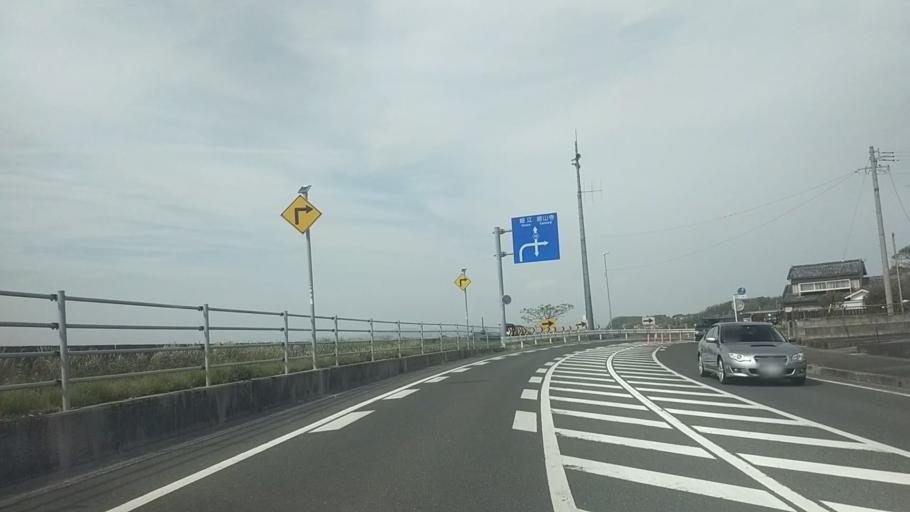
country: JP
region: Shizuoka
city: Kosai-shi
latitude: 34.7146
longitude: 137.6200
